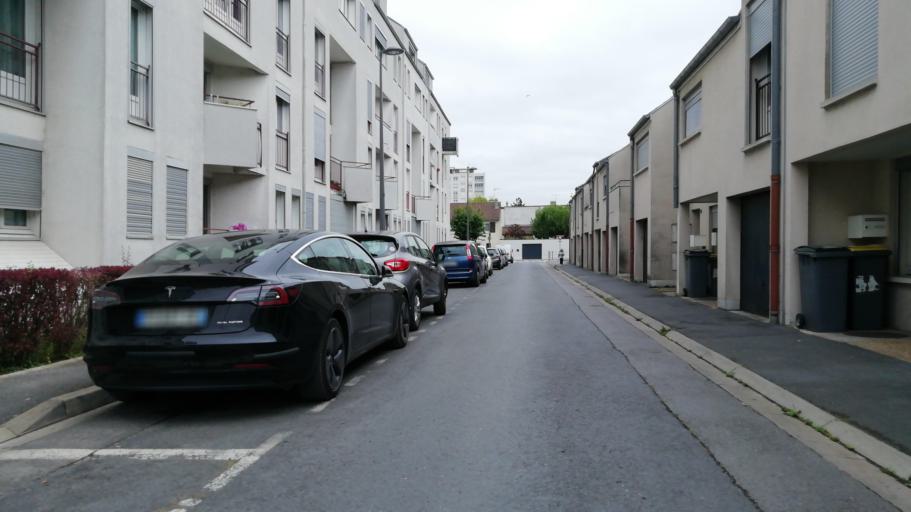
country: FR
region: Champagne-Ardenne
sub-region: Departement de la Marne
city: Betheny
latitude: 49.2636
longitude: 4.0596
